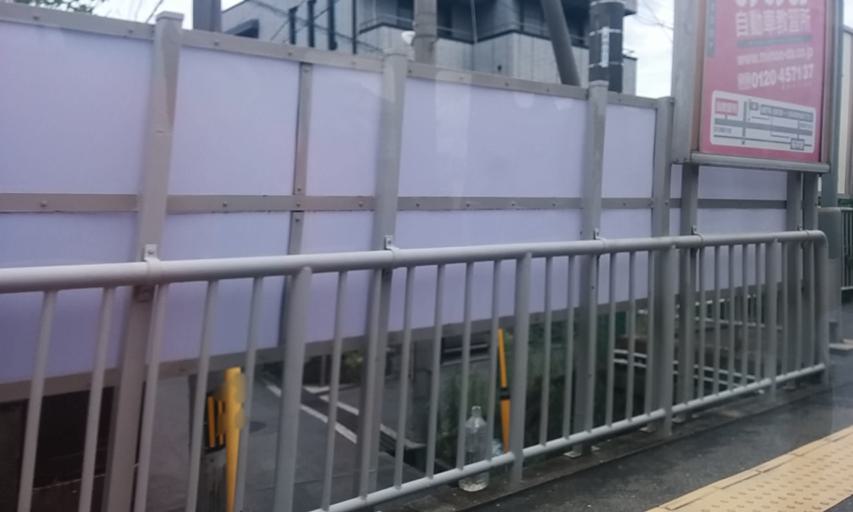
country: JP
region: Osaka
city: Mino
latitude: 34.8164
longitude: 135.4601
